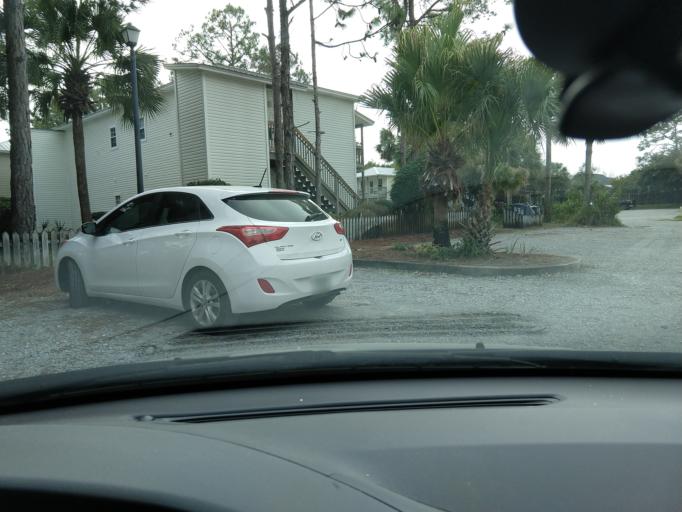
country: US
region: Florida
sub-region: Walton County
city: Miramar Beach
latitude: 30.3921
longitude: -86.3076
